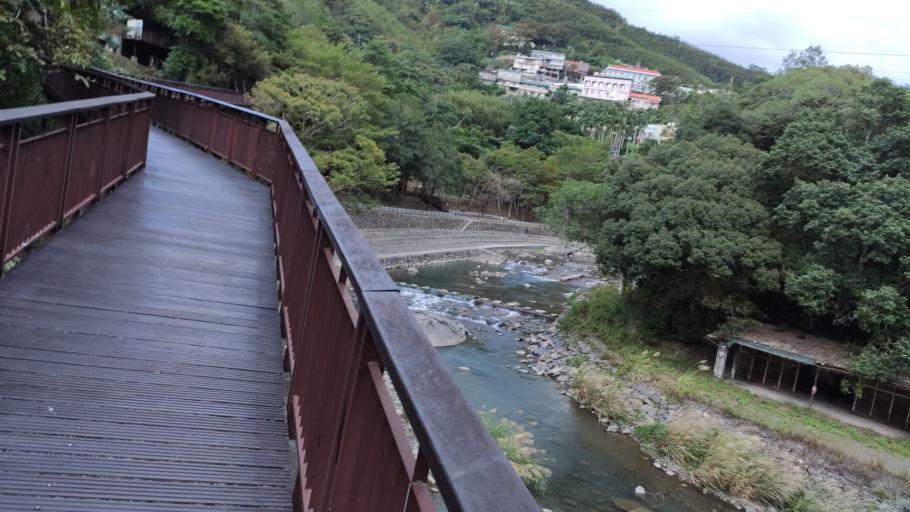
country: TW
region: Taiwan
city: Daxi
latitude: 24.7906
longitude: 121.3760
